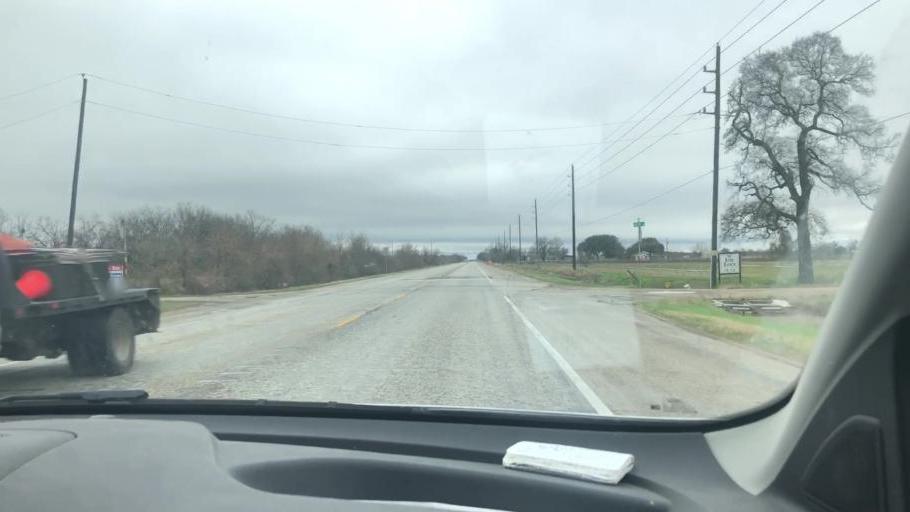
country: US
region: Texas
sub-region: Wharton County
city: Wharton
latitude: 29.2723
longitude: -96.0612
